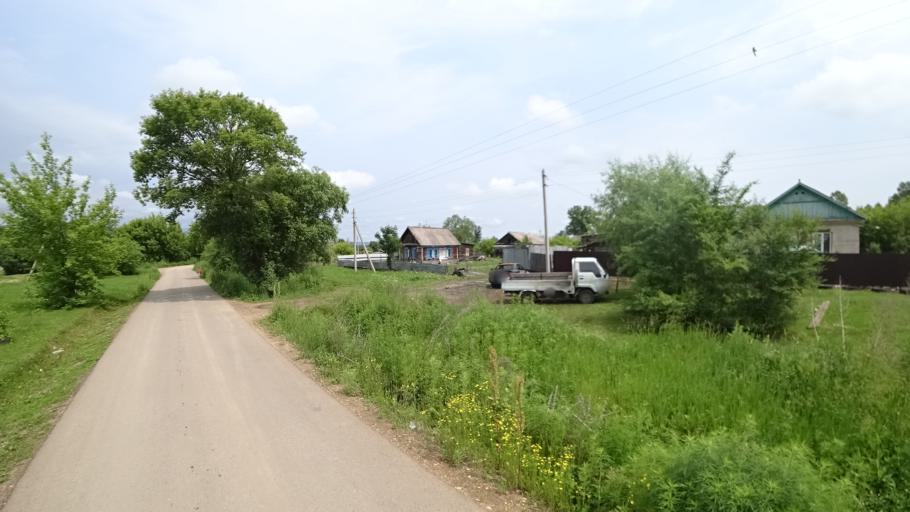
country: RU
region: Primorskiy
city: Novosysoyevka
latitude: 44.2382
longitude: 133.3582
